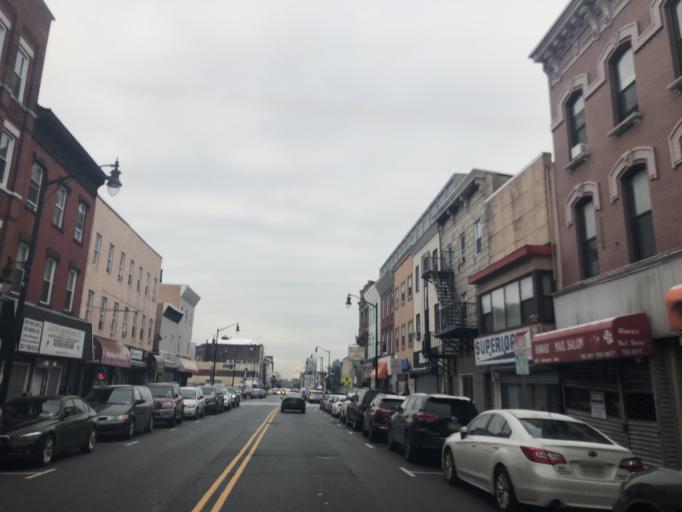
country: US
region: New Jersey
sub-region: Hudson County
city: Jersey City
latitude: 40.7339
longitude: -74.0585
